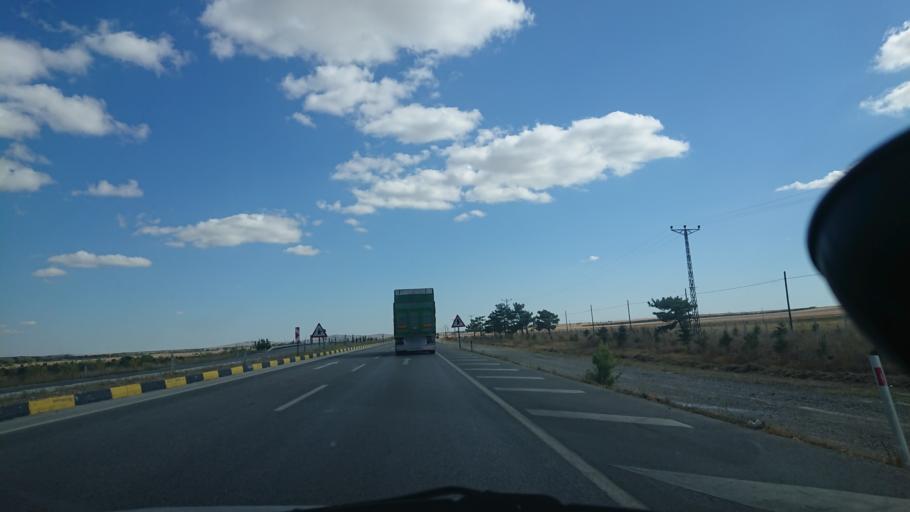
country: TR
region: Eskisehir
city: Mahmudiye
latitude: 39.5570
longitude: 30.9199
